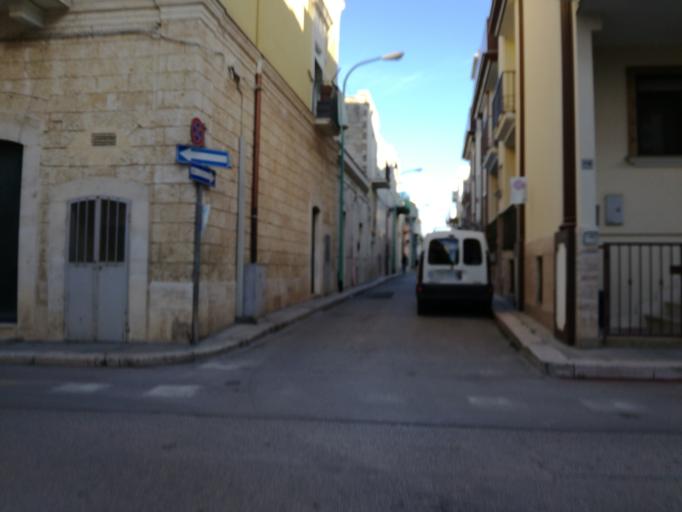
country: IT
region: Apulia
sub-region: Provincia di Bari
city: Adelfia
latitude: 41.0012
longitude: 16.8673
